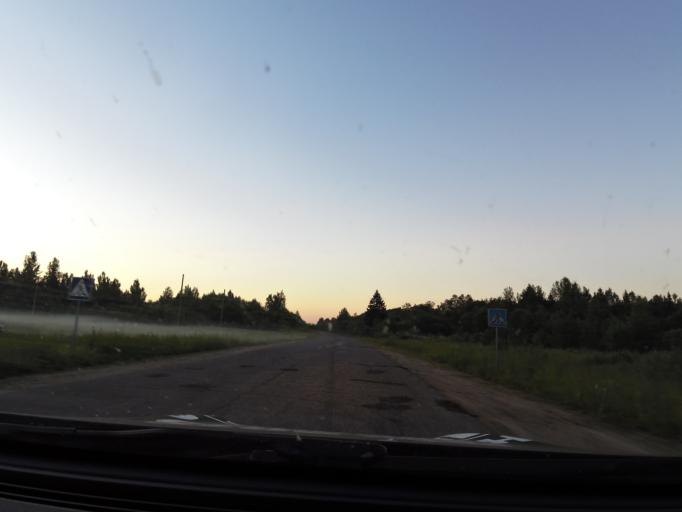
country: RU
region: Kostroma
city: Buy
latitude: 58.3897
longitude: 41.2230
